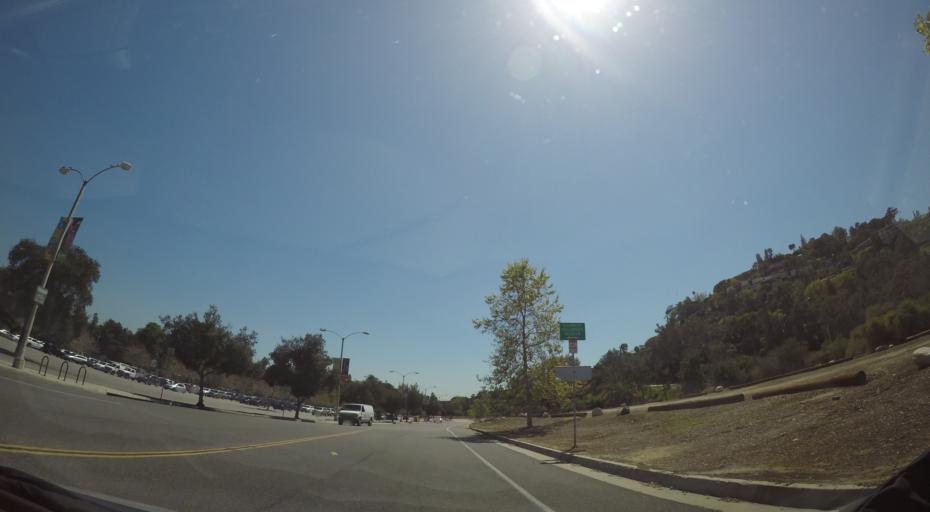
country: US
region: California
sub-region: Los Angeles County
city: Pasadena
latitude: 34.1558
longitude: -118.1673
